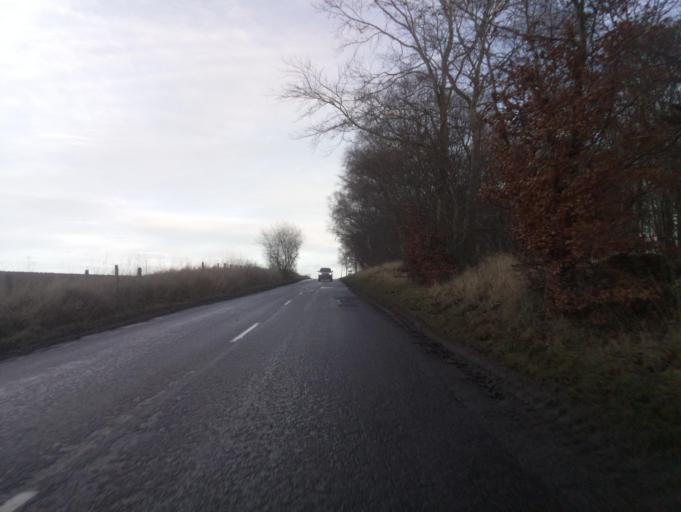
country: GB
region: Scotland
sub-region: Angus
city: Forfar
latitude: 56.5865
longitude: -2.8576
